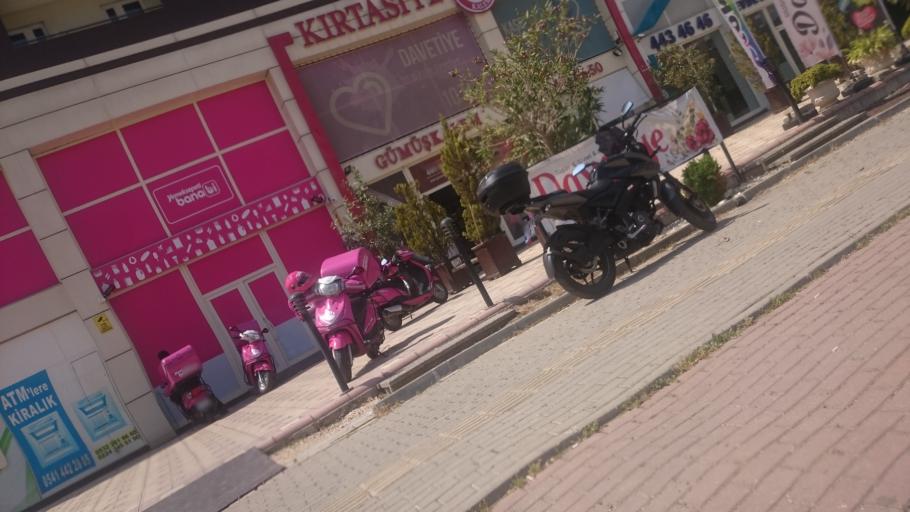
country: TR
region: Bursa
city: Cali
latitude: 40.2183
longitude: 28.9520
